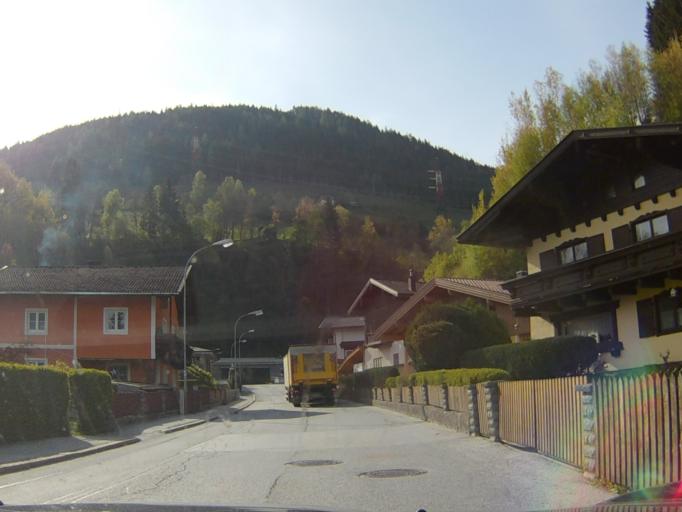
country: AT
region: Salzburg
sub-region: Politischer Bezirk Zell am See
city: Mittersill
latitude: 47.2743
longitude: 12.4844
